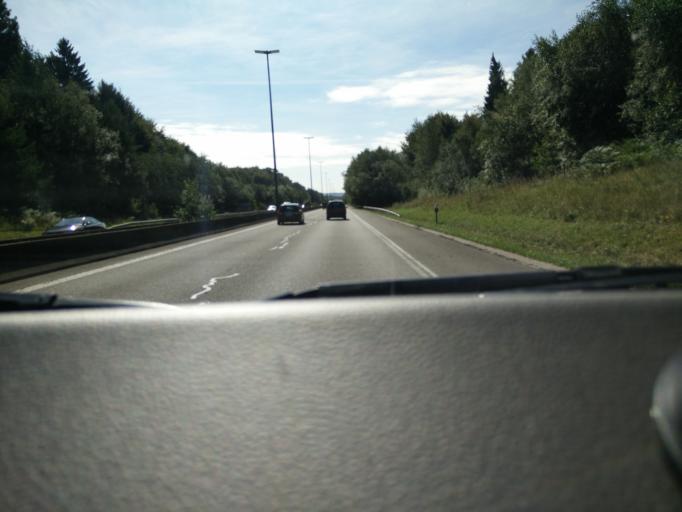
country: BE
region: Wallonia
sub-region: Province du Luxembourg
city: Libin
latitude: 49.9961
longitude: 5.2272
